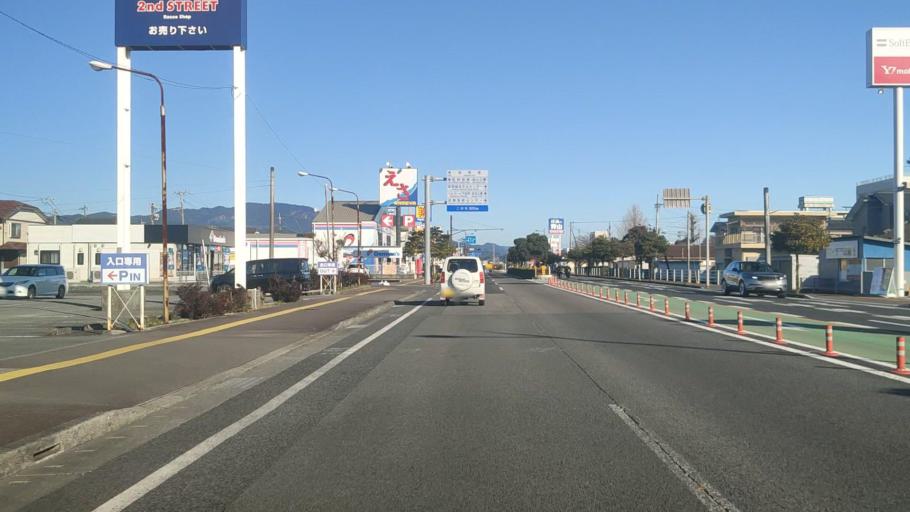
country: JP
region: Miyazaki
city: Nobeoka
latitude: 32.5721
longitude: 131.6836
